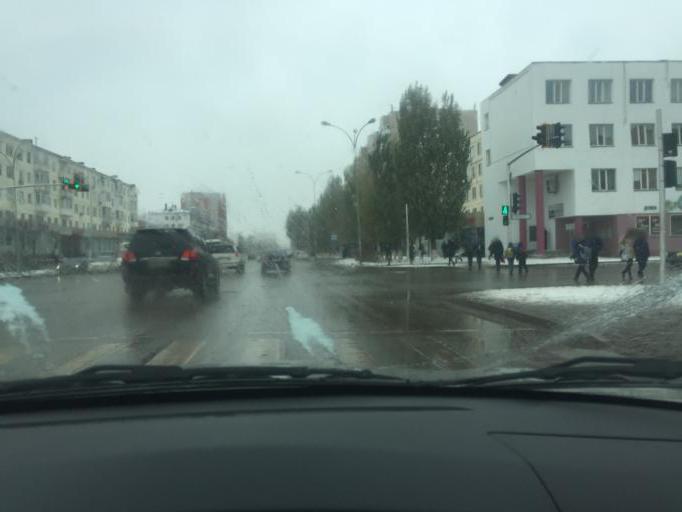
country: KZ
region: Astana Qalasy
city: Astana
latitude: 51.1697
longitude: 71.4129
